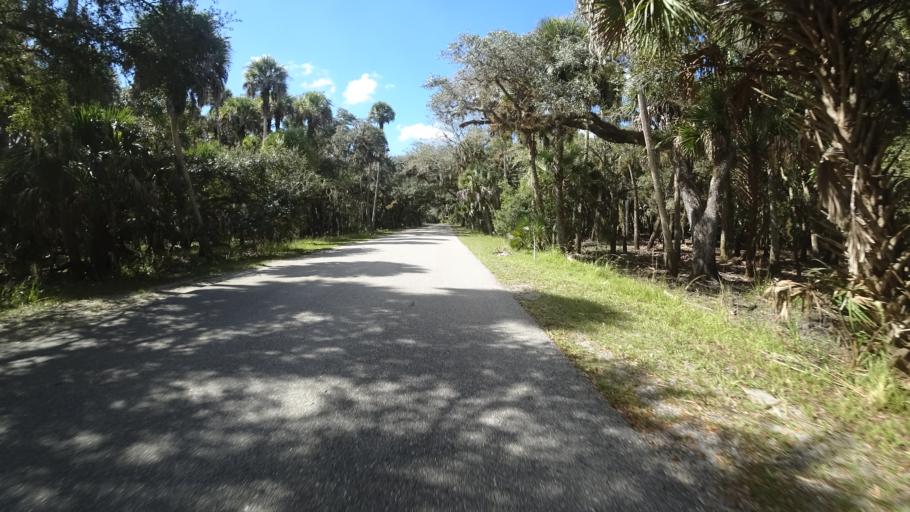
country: US
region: Florida
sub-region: Sarasota County
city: Lake Sarasota
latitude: 27.2475
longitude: -82.2973
